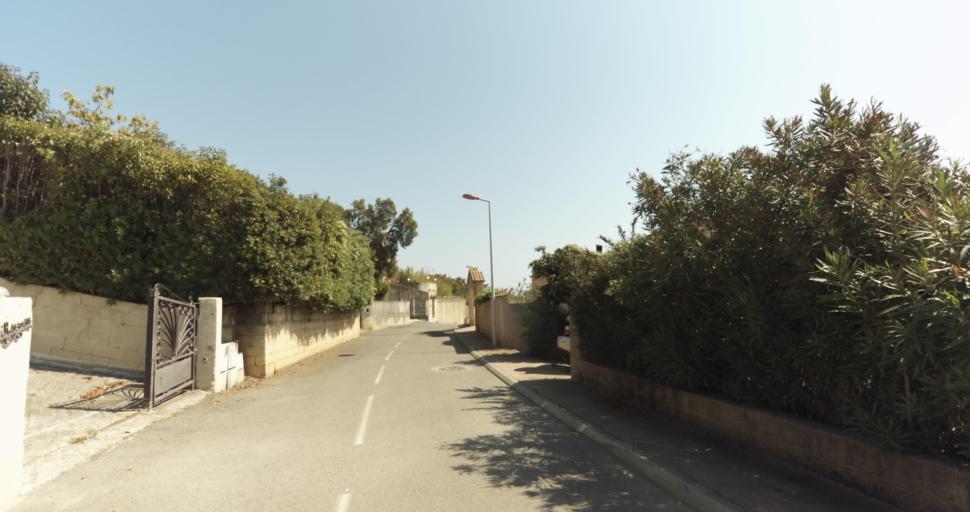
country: FR
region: Corsica
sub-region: Departement de la Haute-Corse
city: Biguglia
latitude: 42.6206
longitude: 9.4256
